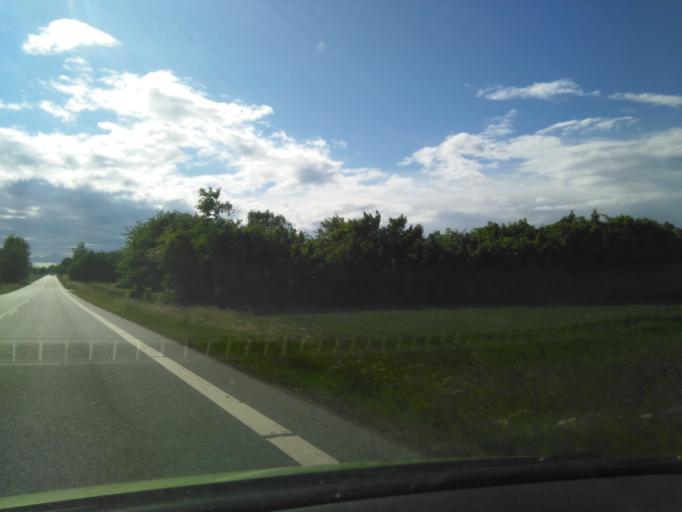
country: DK
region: Capital Region
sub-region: Bornholm Kommune
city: Nexo
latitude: 55.1389
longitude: 15.0305
